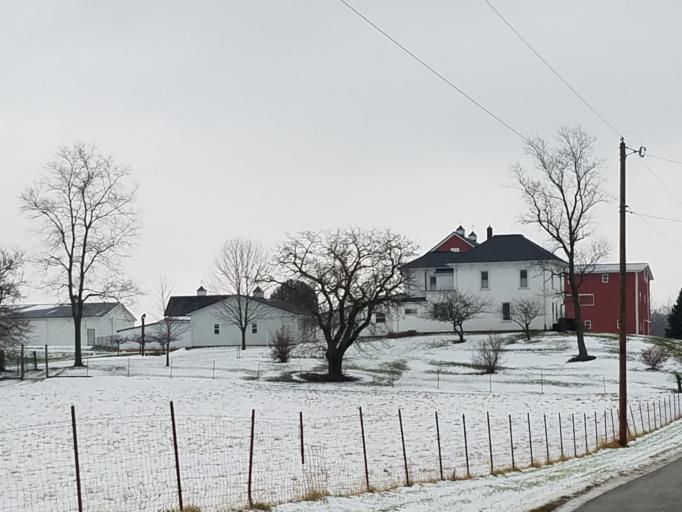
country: US
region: Ohio
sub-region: Morrow County
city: Mount Gilead
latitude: 40.5370
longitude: -82.7553
